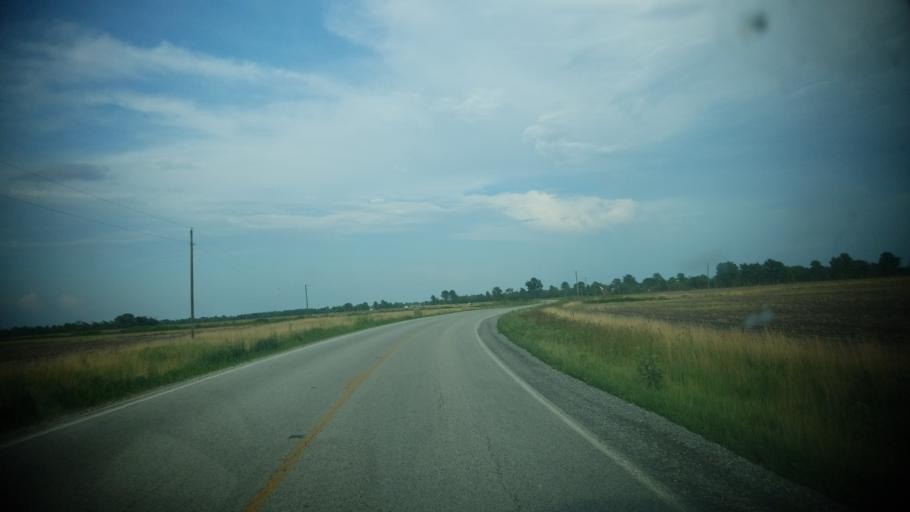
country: US
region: Illinois
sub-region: Clay County
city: Flora
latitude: 38.5172
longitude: -88.4729
